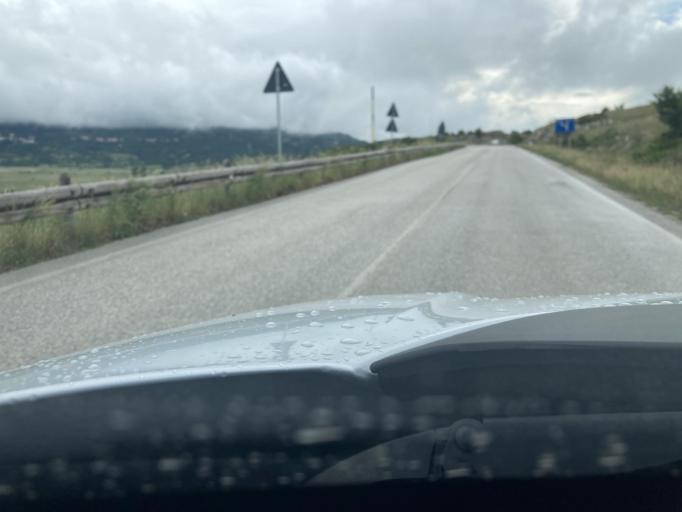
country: IT
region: Abruzzo
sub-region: Provincia dell' Aquila
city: Villa Sant'Angelo
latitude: 42.2372
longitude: 13.5295
